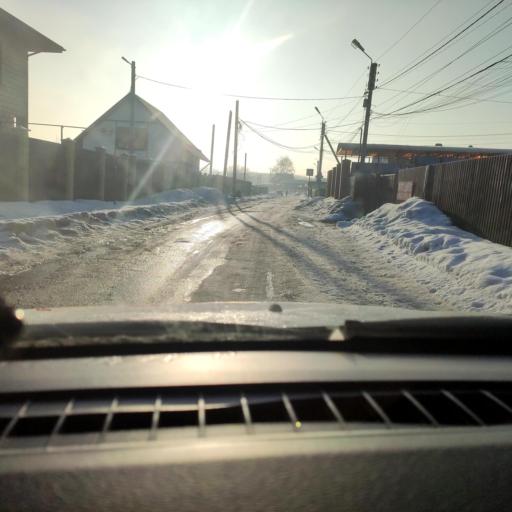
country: RU
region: Samara
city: Novokuybyshevsk
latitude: 53.1191
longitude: 49.9497
